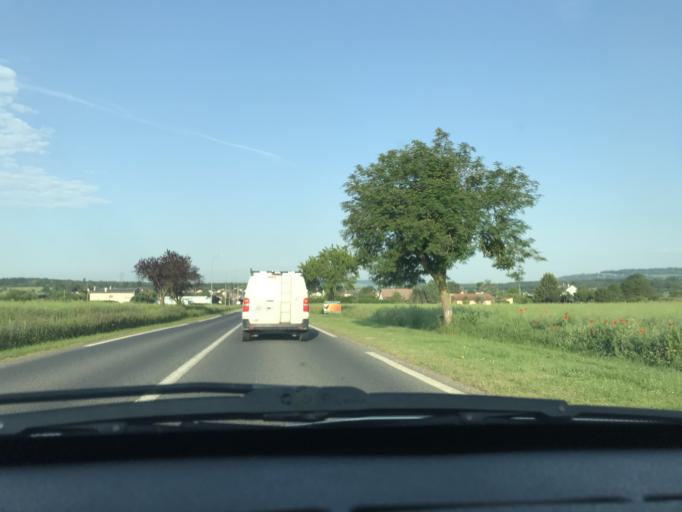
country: FR
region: Lorraine
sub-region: Departement de Meurthe-et-Moselle
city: Champenoux
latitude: 48.7450
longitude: 6.3596
